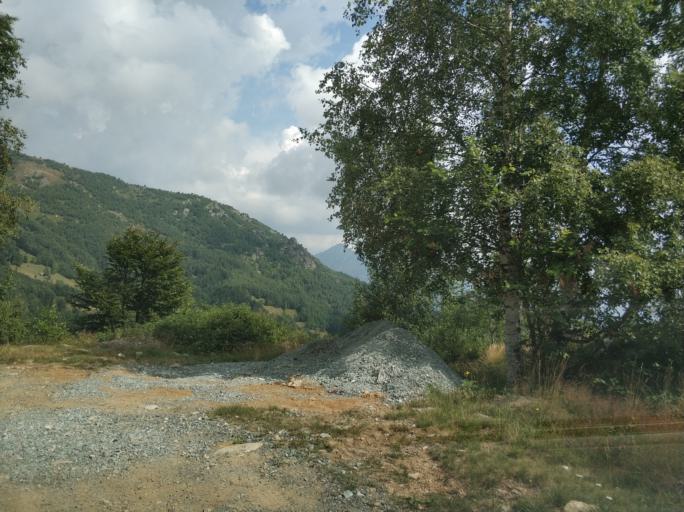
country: IT
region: Piedmont
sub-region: Provincia di Torino
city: Viu
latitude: 45.1965
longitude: 7.3621
